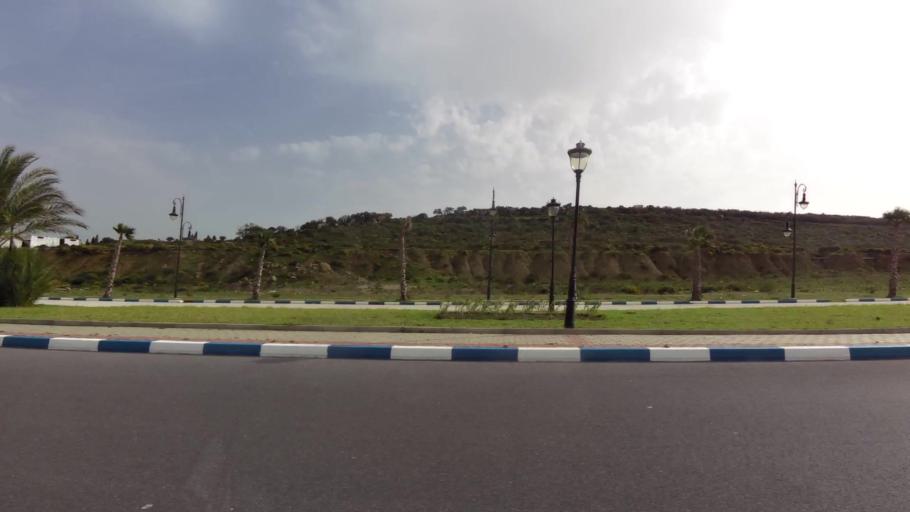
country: MA
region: Tanger-Tetouan
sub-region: Tanger-Assilah
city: Boukhalef
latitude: 35.6973
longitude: -5.9250
